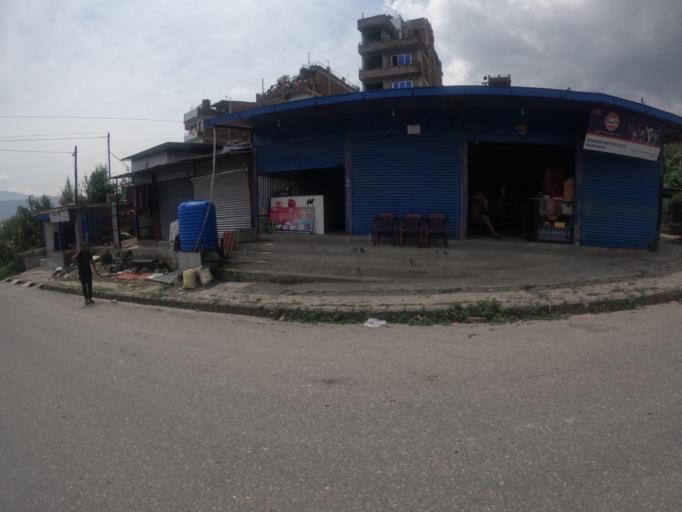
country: NP
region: Central Region
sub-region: Bagmati Zone
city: Bhaktapur
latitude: 27.6807
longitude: 85.3890
